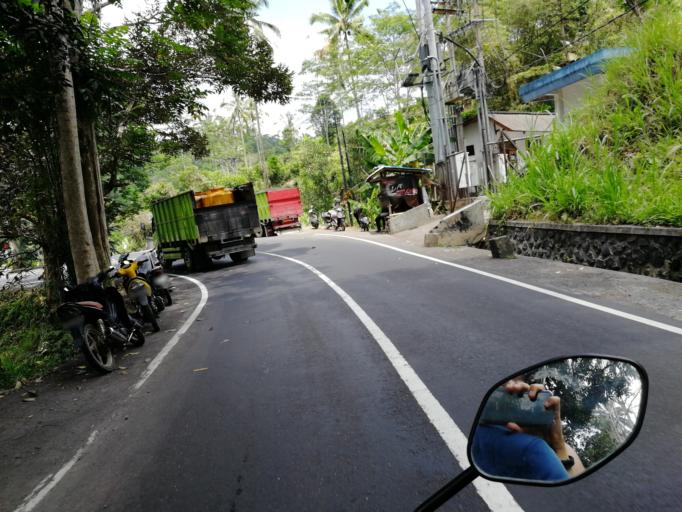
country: ID
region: Bali
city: Banjar Geriana Kangin
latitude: -8.4233
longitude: 115.4340
